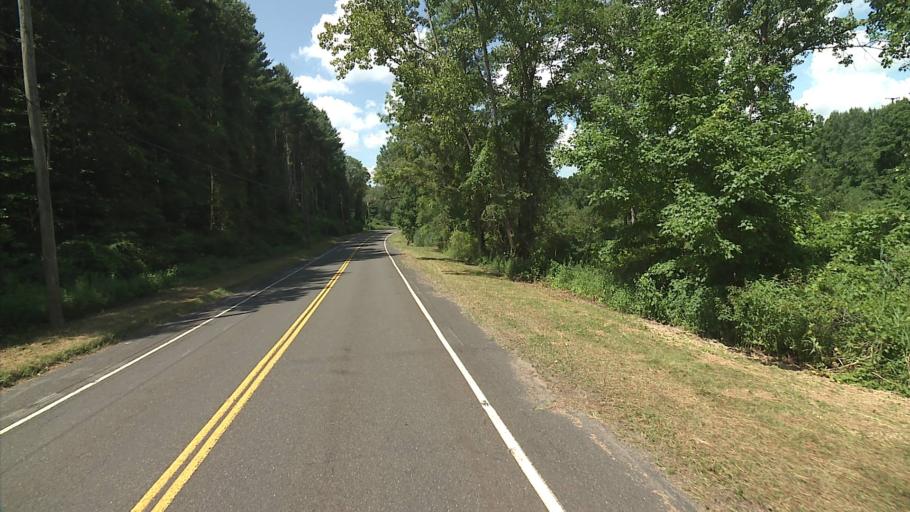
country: US
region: Connecticut
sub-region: Litchfield County
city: Canaan
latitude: 41.9481
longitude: -73.3275
